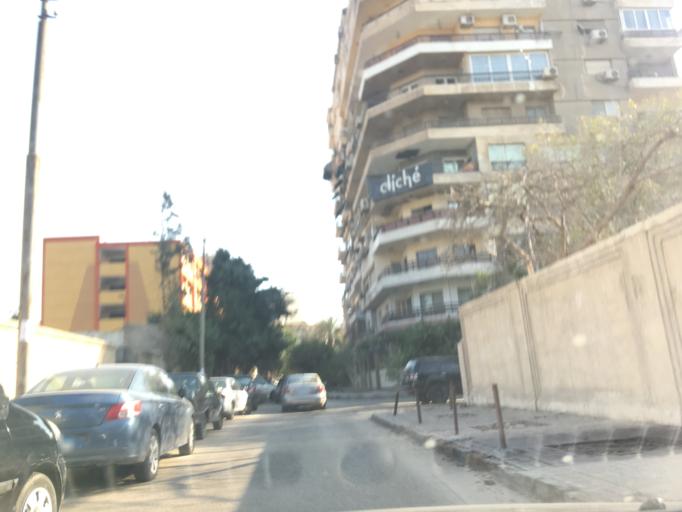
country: EG
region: Muhafazat al Qahirah
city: Cairo
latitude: 30.0892
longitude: 31.3327
